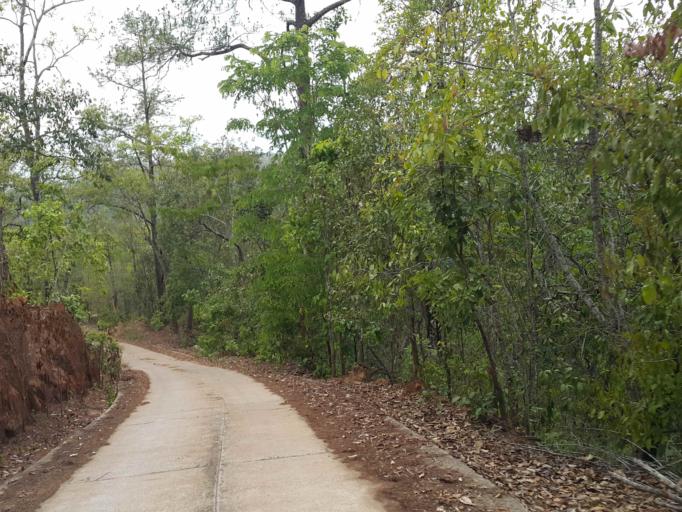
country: TH
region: Chiang Mai
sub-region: Amphoe Chiang Dao
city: Chiang Dao
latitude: 19.3064
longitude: 98.7366
